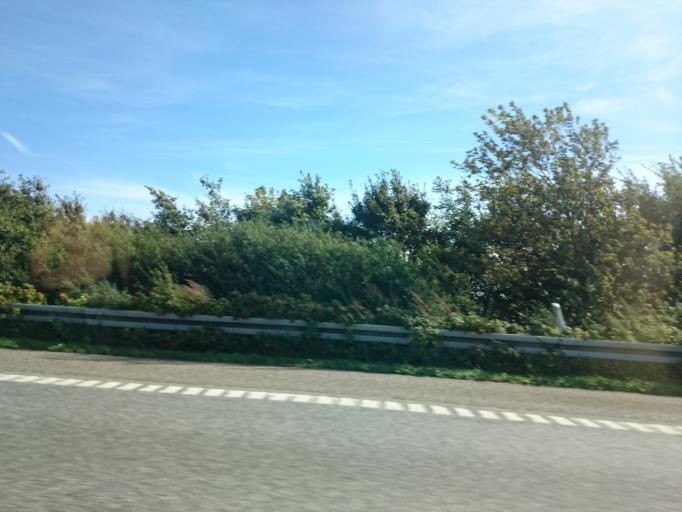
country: DK
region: Central Jutland
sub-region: Skanderborg Kommune
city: Stilling
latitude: 56.0796
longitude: 10.0080
